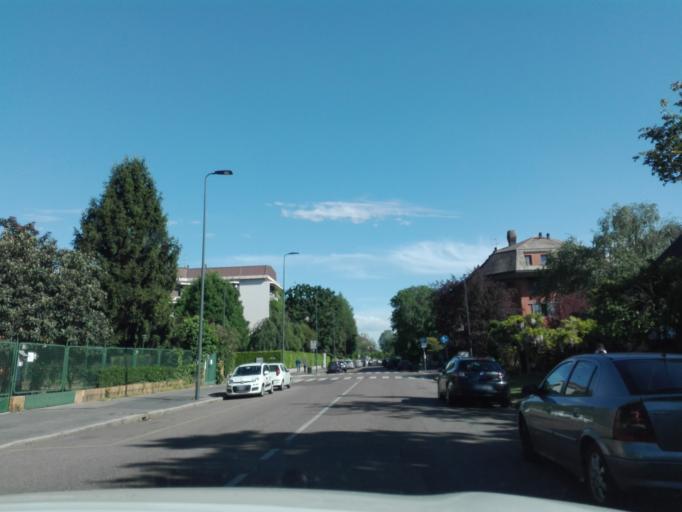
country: IT
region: Lombardy
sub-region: Citta metropolitana di Milano
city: Romano Banco
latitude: 45.4784
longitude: 9.1347
